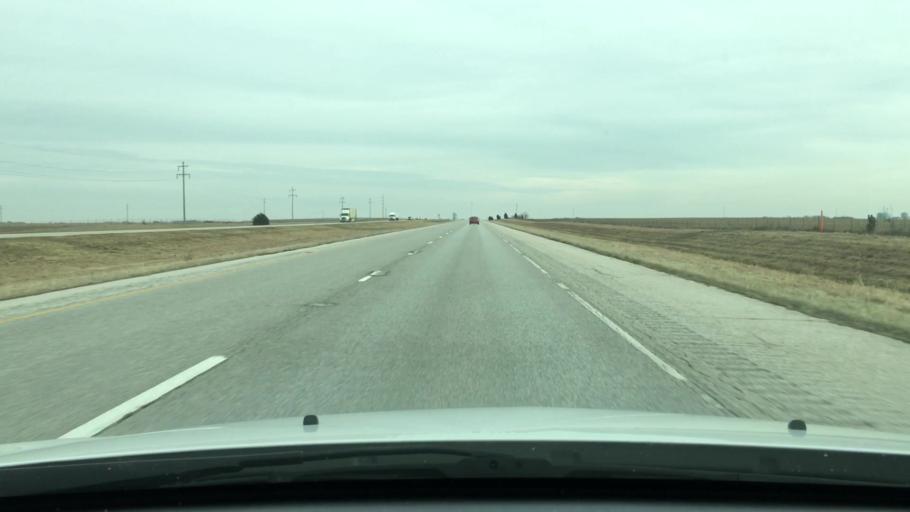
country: US
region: Illinois
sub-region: Morgan County
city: Jacksonville
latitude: 39.7379
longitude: -90.1198
